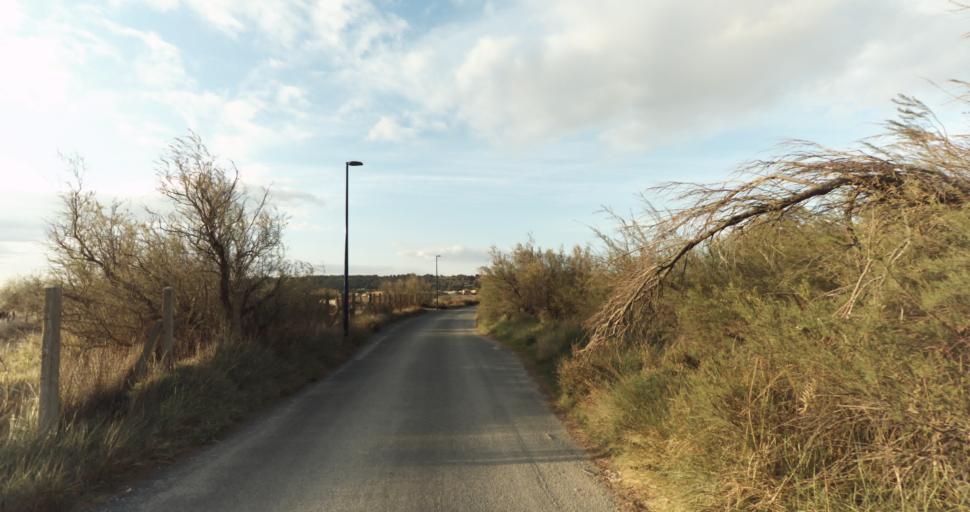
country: FR
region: Languedoc-Roussillon
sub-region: Departement de l'Aude
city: Leucate
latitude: 42.9425
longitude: 3.0280
